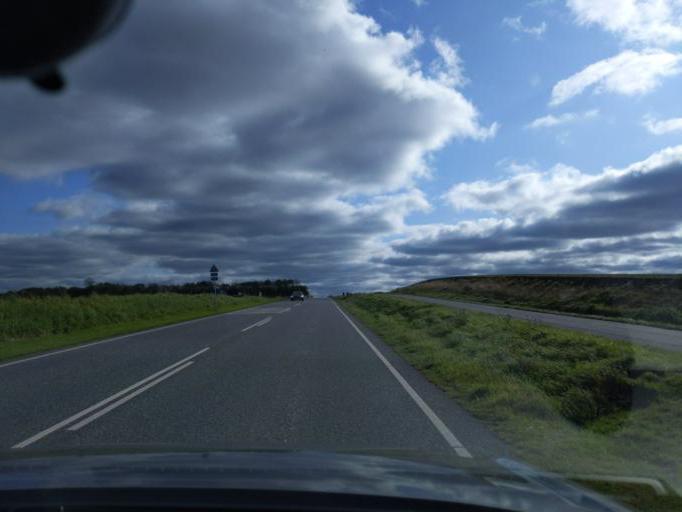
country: DK
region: North Denmark
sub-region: Mariagerfjord Kommune
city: Hobro
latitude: 56.5232
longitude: 9.7312
